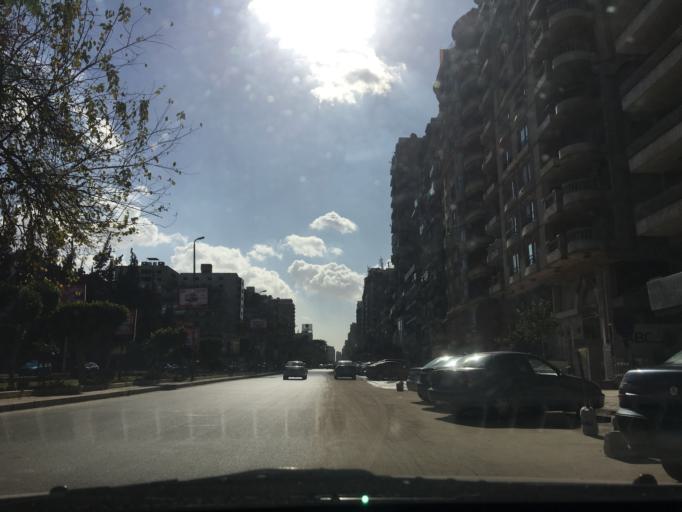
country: EG
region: Muhafazat al Qahirah
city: Cairo
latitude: 30.0618
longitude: 31.3450
